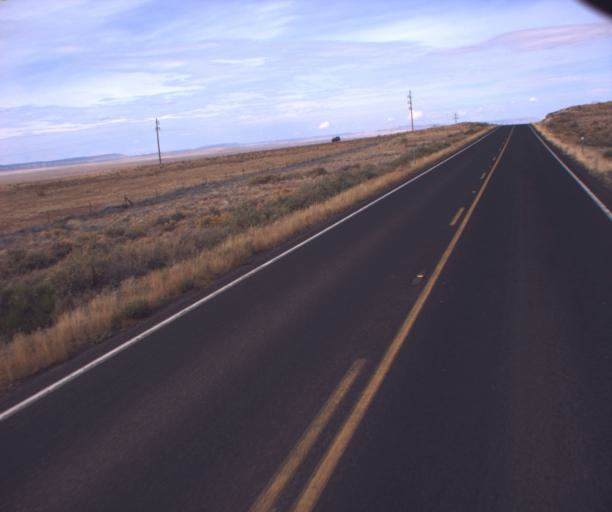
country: US
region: Arizona
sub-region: Apache County
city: Ganado
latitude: 35.8804
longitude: -109.6030
